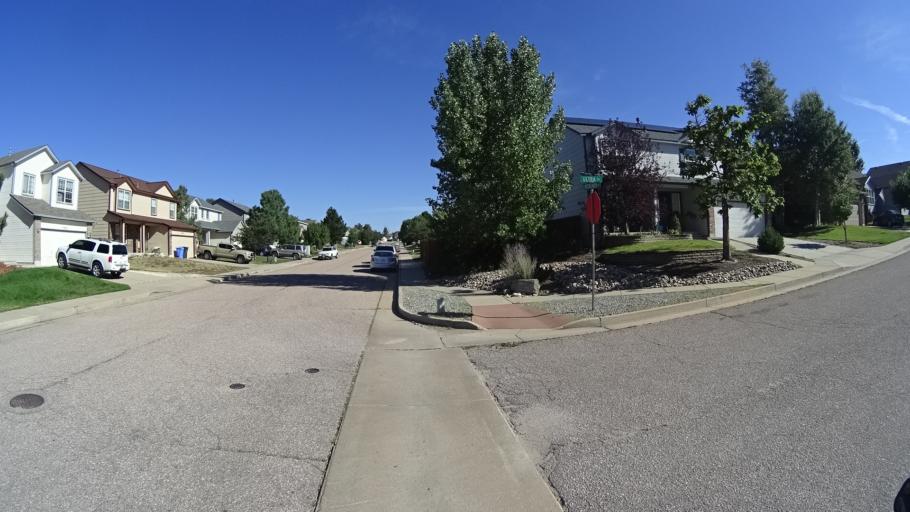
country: US
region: Colorado
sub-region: El Paso County
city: Black Forest
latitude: 38.9465
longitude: -104.7375
